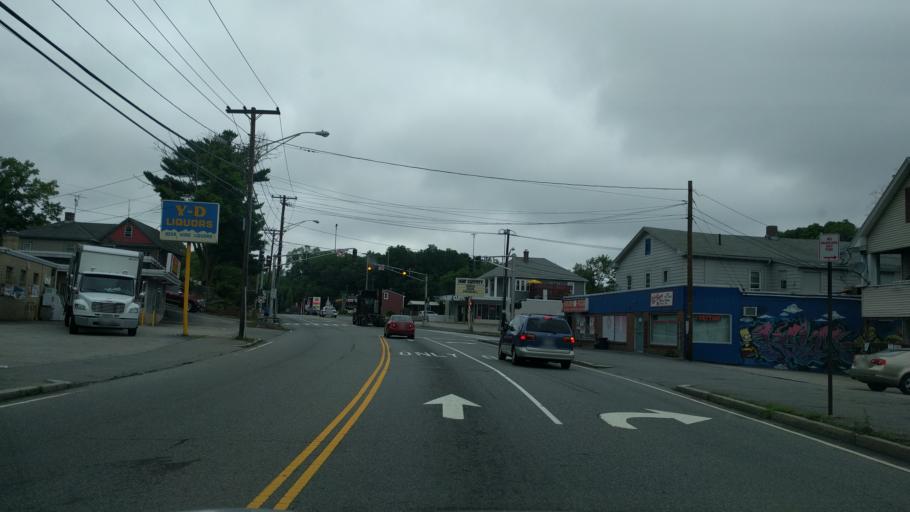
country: US
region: Massachusetts
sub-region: Worcester County
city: Sunderland
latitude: 42.2406
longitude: -71.7536
